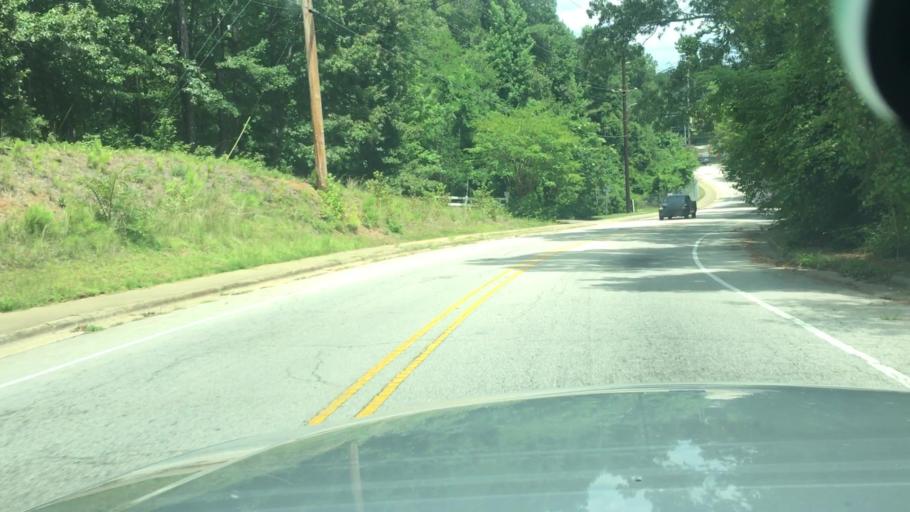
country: US
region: North Carolina
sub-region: Cumberland County
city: Fayetteville
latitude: 35.0677
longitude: -78.8989
